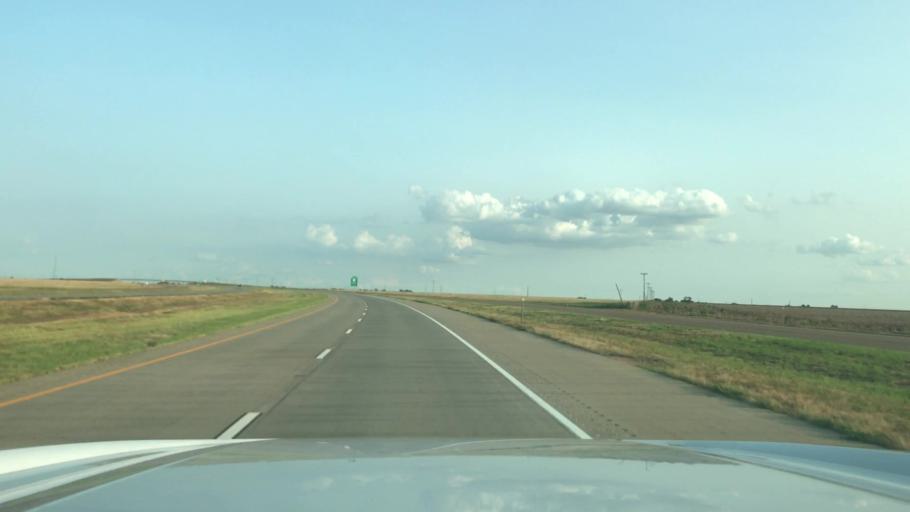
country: US
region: Texas
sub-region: Swisher County
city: Tulia
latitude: 34.3826
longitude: -101.7765
